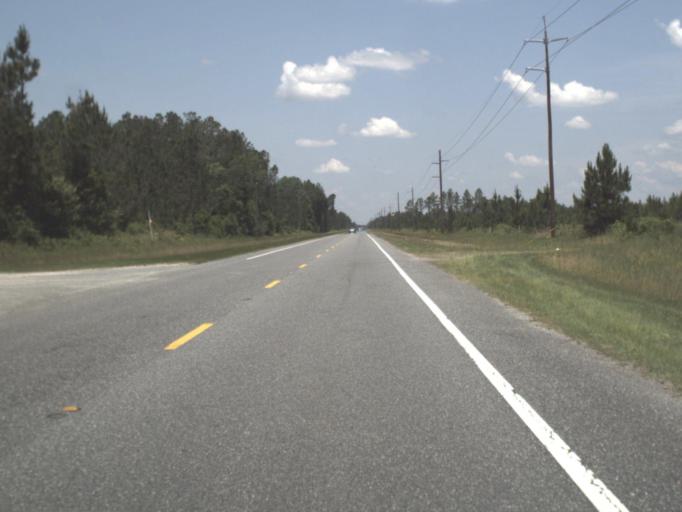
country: US
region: Florida
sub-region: Bradford County
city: Starke
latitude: 29.9699
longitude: -82.2063
